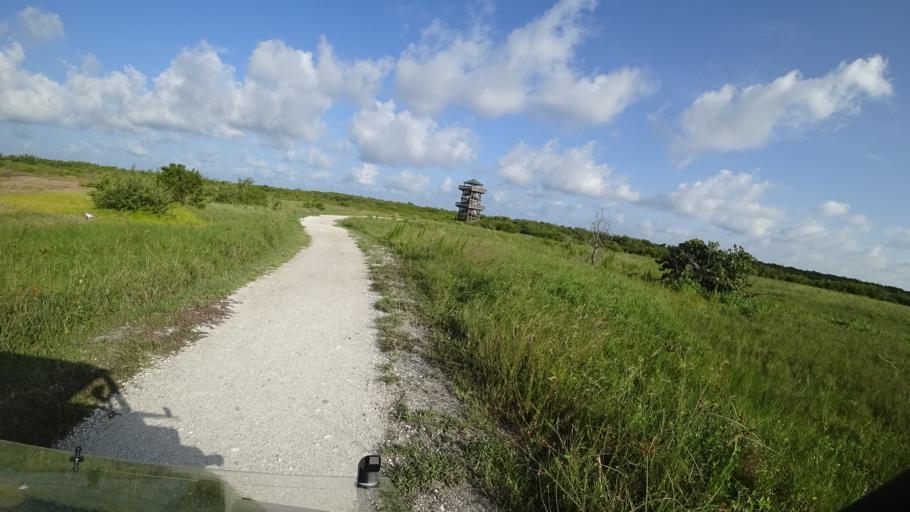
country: US
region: Florida
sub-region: Manatee County
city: West Bradenton
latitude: 27.5181
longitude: -82.6639
